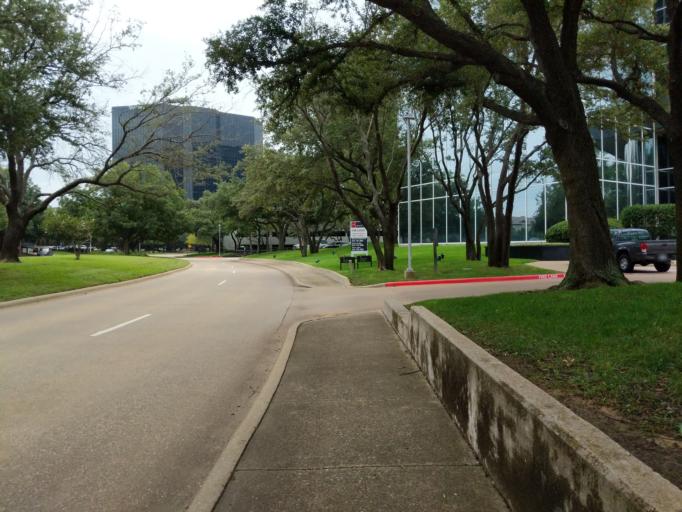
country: US
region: Texas
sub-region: Dallas County
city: Richardson
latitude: 32.9166
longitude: -96.7728
